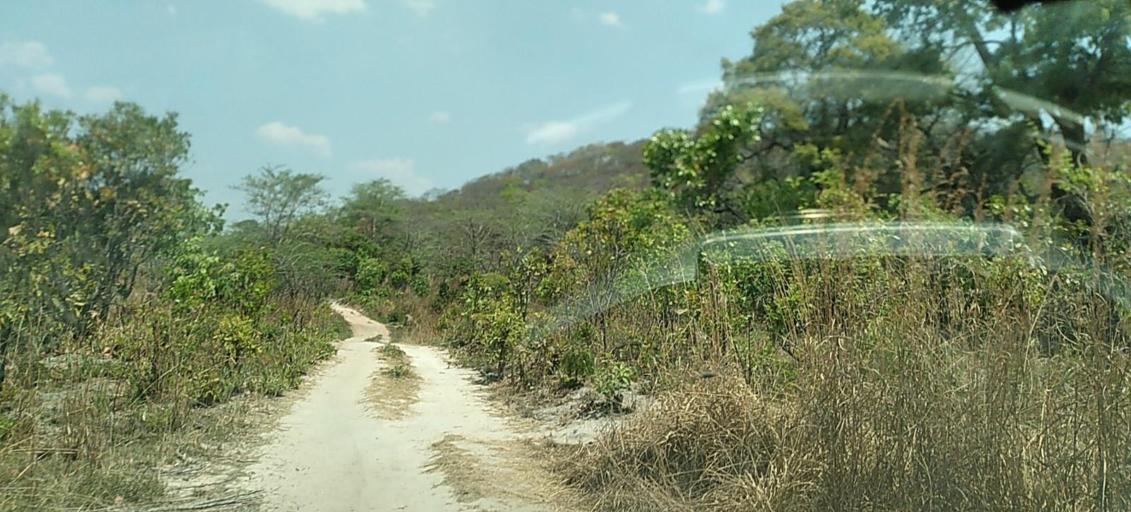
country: ZM
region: North-Western
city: Kasempa
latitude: -13.5275
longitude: 25.8224
